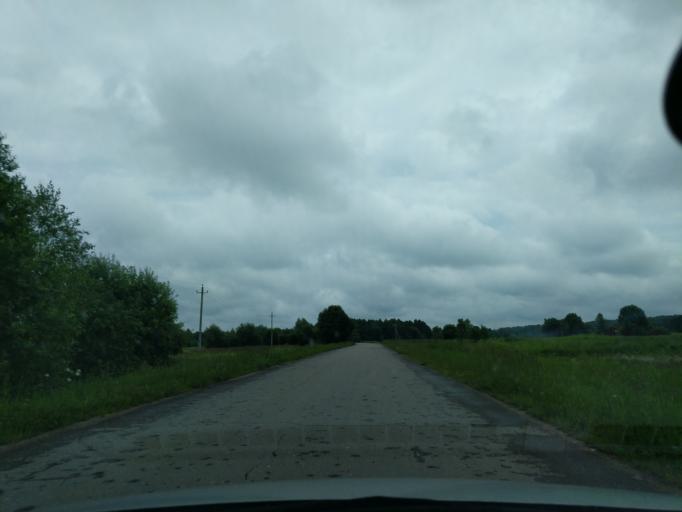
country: RU
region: Kaluga
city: Myatlevo
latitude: 54.8377
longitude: 35.6353
